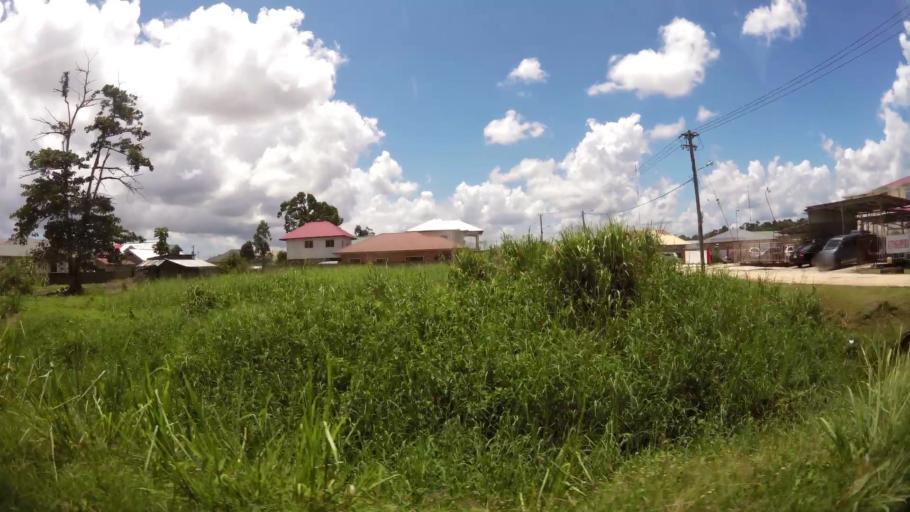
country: SR
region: Paramaribo
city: Paramaribo
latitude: 5.8546
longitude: -55.1665
